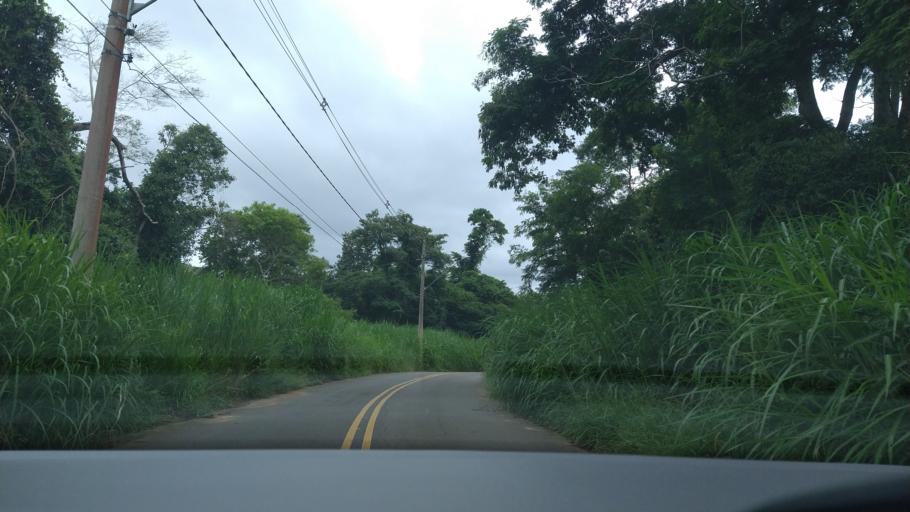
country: BR
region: Minas Gerais
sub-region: Vicosa
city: Vicosa
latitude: -20.7766
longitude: -42.8628
